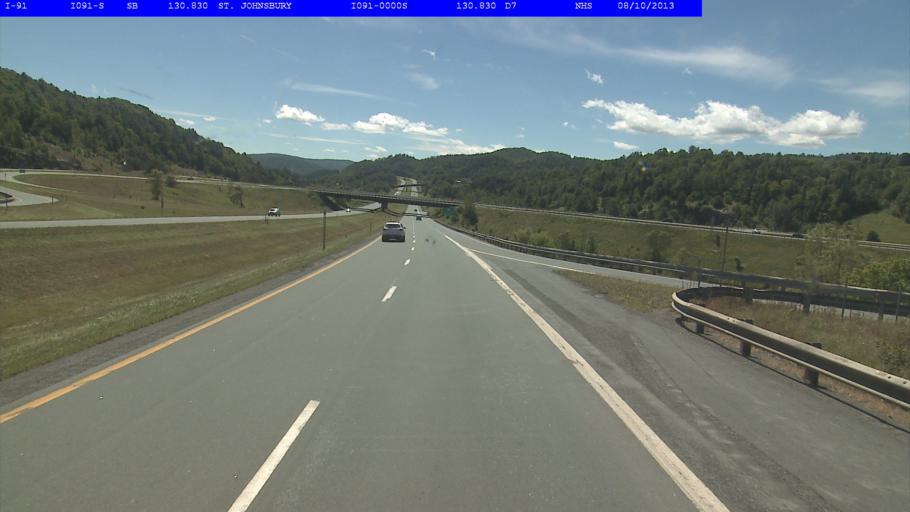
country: US
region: Vermont
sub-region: Caledonia County
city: St Johnsbury
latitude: 44.4311
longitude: -72.0345
